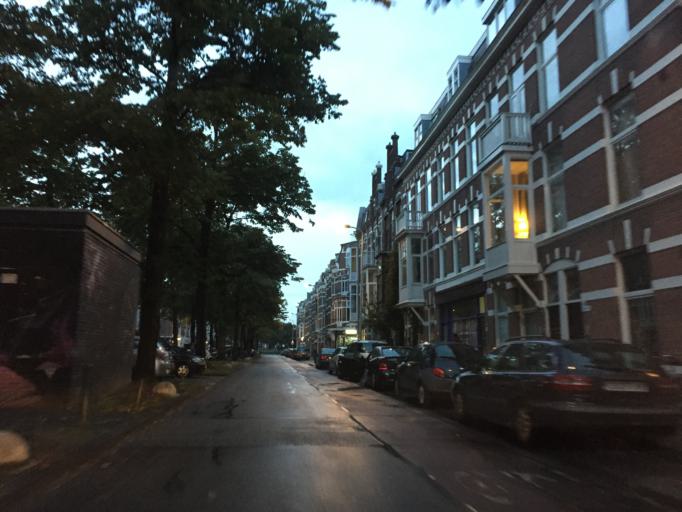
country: NL
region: South Holland
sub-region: Gemeente Den Haag
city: The Hague
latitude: 52.0748
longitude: 4.2836
